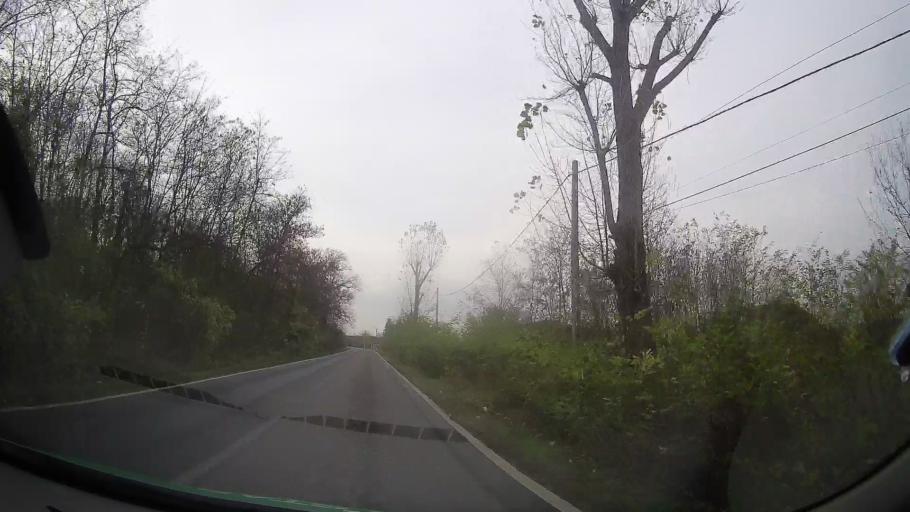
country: RO
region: Prahova
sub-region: Comuna Balta Doamnei
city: Balta Doamnei
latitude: 44.7436
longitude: 26.1331
